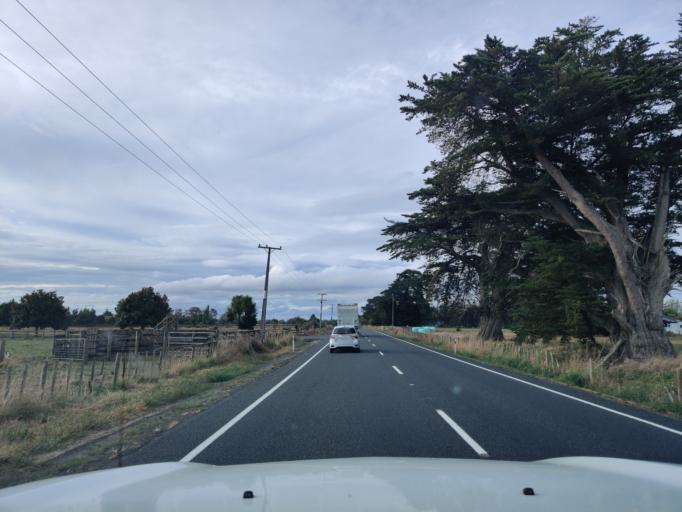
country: NZ
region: Waikato
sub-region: Hamilton City
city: Hamilton
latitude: -37.6980
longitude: 175.3381
